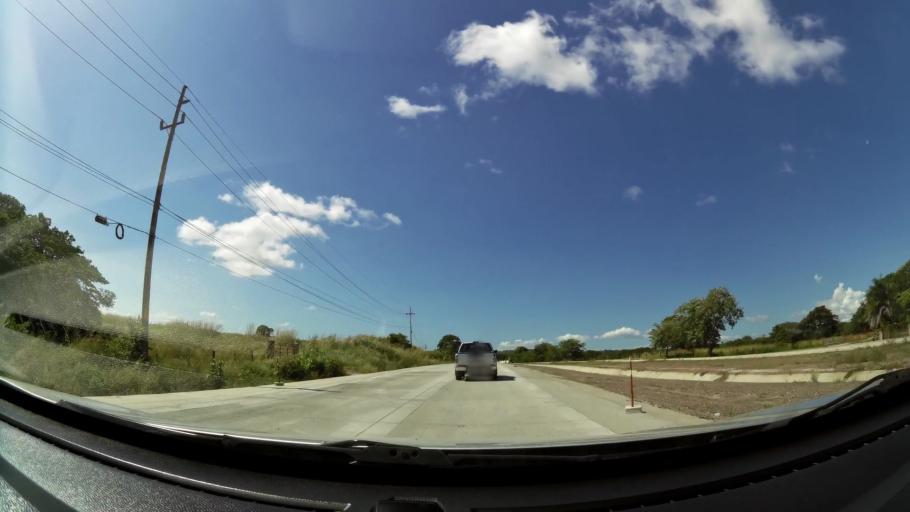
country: CR
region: Guanacaste
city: Bagaces
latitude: 10.5388
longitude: -85.3022
